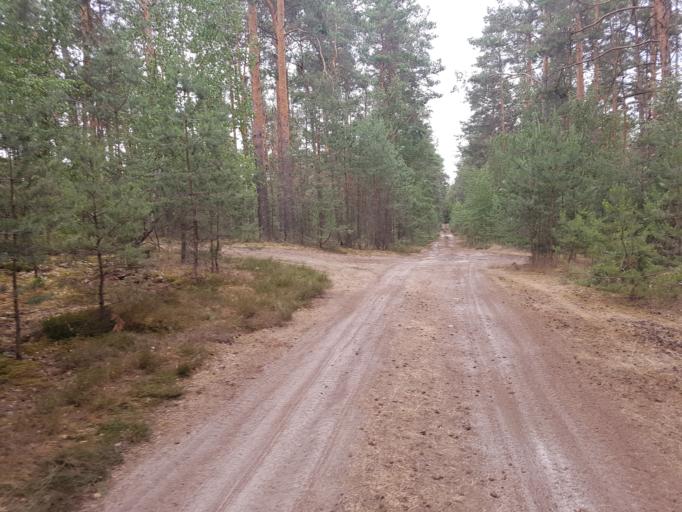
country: DE
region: Brandenburg
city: Finsterwalde
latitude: 51.6309
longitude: 13.6622
